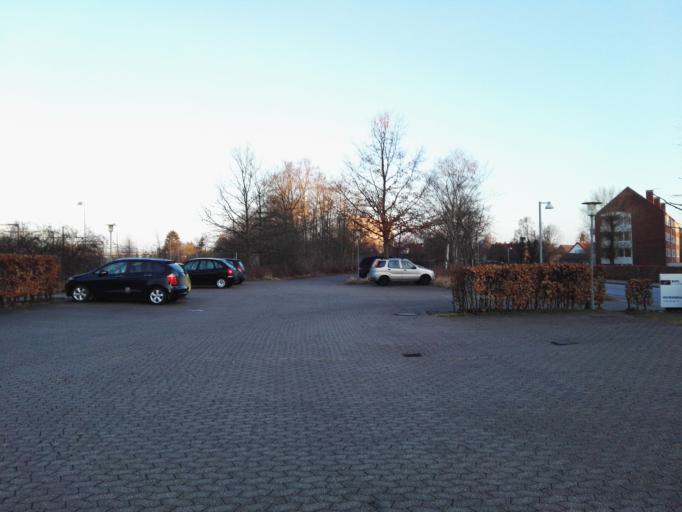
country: DK
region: Capital Region
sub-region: Ballerup Kommune
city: Ballerup
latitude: 55.7316
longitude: 12.3552
